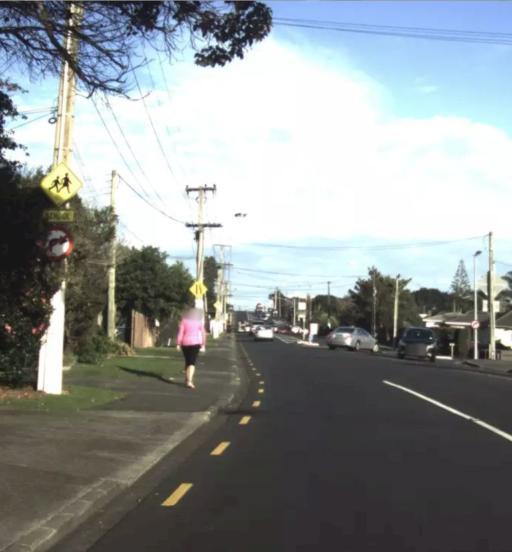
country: NZ
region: Auckland
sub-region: Auckland
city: Waitakere
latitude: -36.9213
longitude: 174.7177
